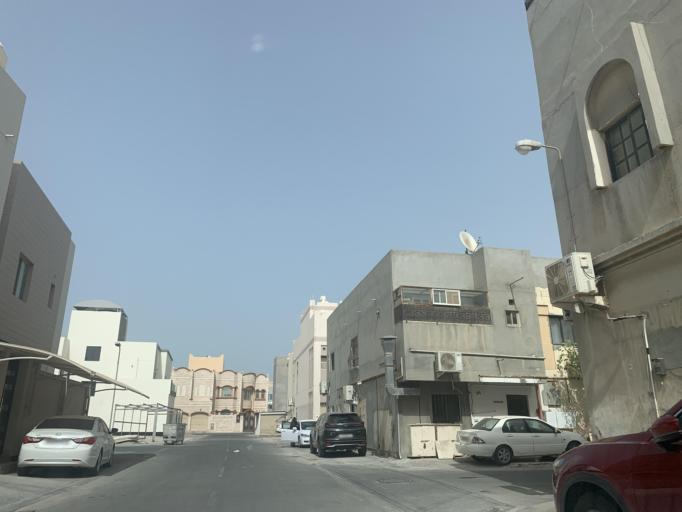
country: BH
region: Northern
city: Sitrah
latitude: 26.1713
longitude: 50.6218
